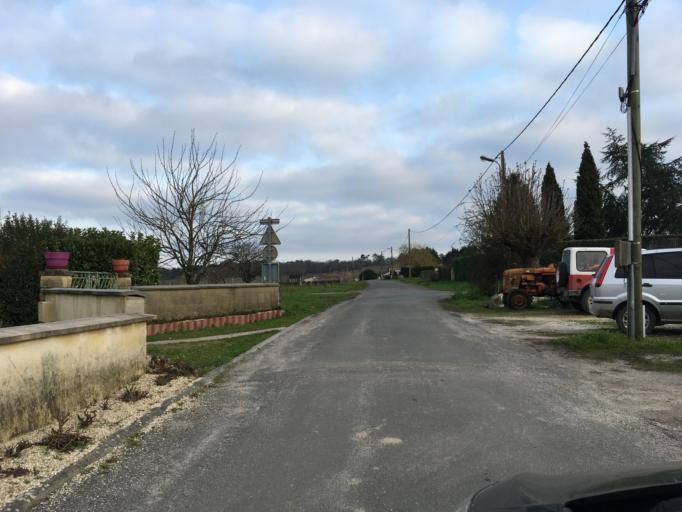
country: FR
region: Aquitaine
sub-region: Departement de la Gironde
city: Saint-Ciers-sur-Gironde
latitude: 45.3151
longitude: -0.6169
